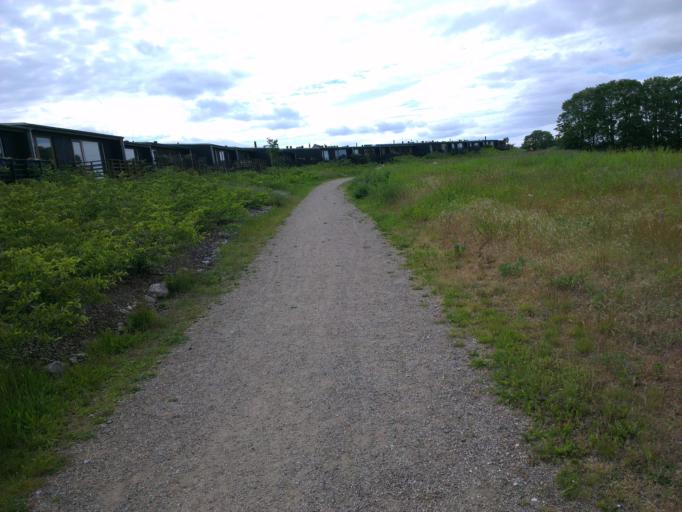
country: DK
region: Capital Region
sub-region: Frederikssund Kommune
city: Frederikssund
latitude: 55.8651
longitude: 12.0779
